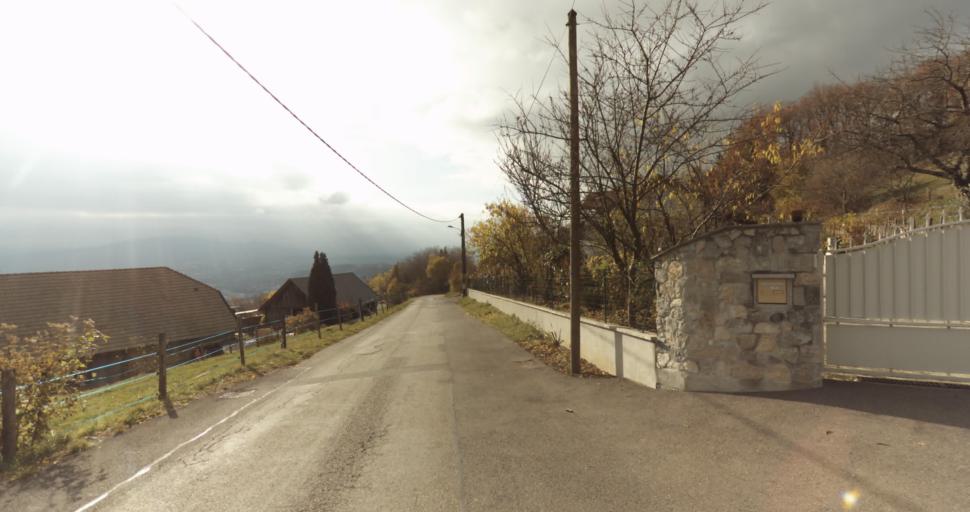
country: FR
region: Rhone-Alpes
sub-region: Departement de la Haute-Savoie
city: Epagny
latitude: 45.9548
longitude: 6.0776
